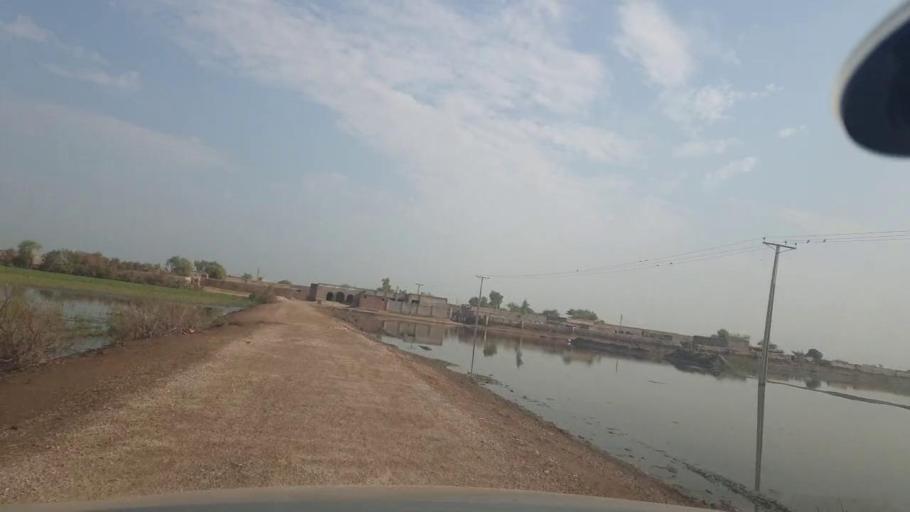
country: PK
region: Balochistan
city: Mehrabpur
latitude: 28.0725
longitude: 68.2110
